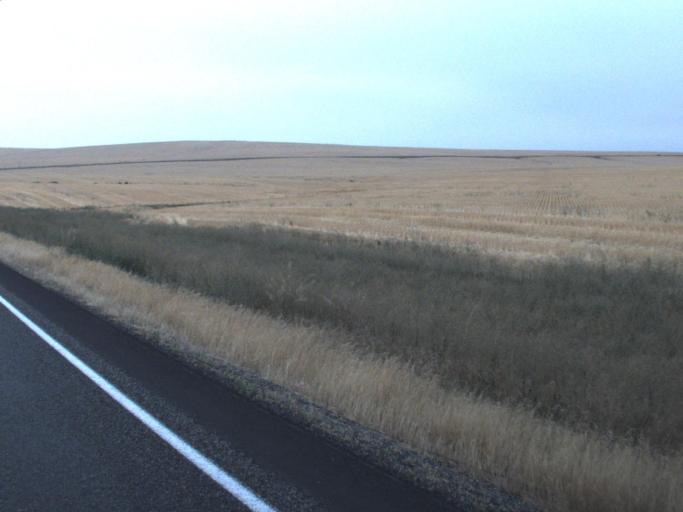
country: US
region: Washington
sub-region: Benton County
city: Prosser
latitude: 46.1873
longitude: -119.6872
